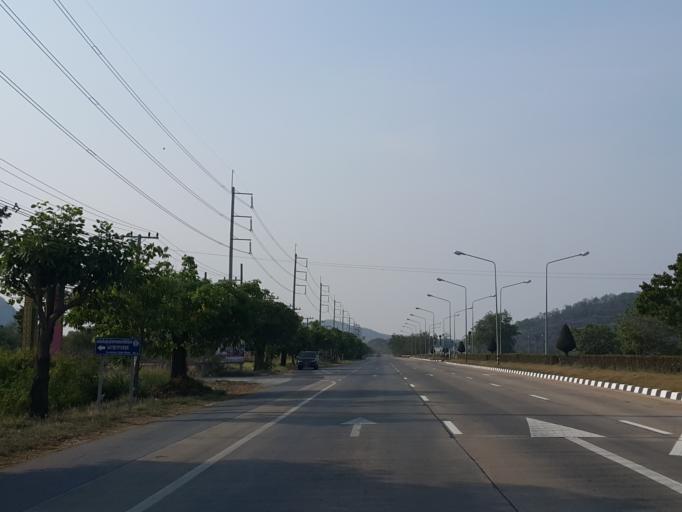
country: TH
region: Suphan Buri
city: Doembang Nangbuat
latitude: 14.8233
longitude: 100.1150
